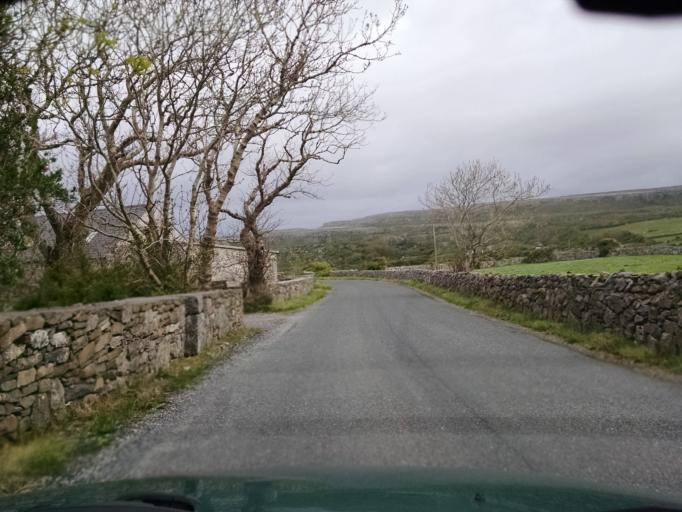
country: IE
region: Connaught
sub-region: County Galway
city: Bearna
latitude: 53.0510
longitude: -9.3416
